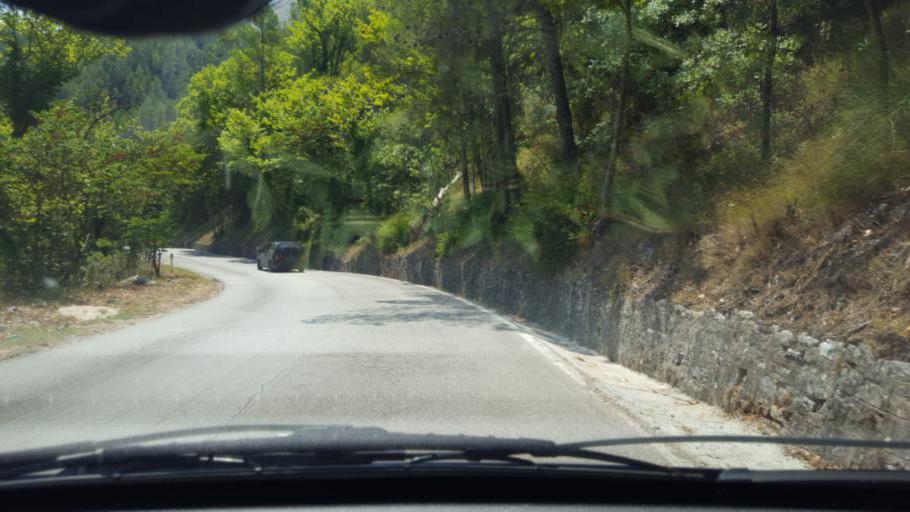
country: AL
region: Vlore
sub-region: Rrethi i Delvines
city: Delvine
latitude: 39.9223
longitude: 20.1643
